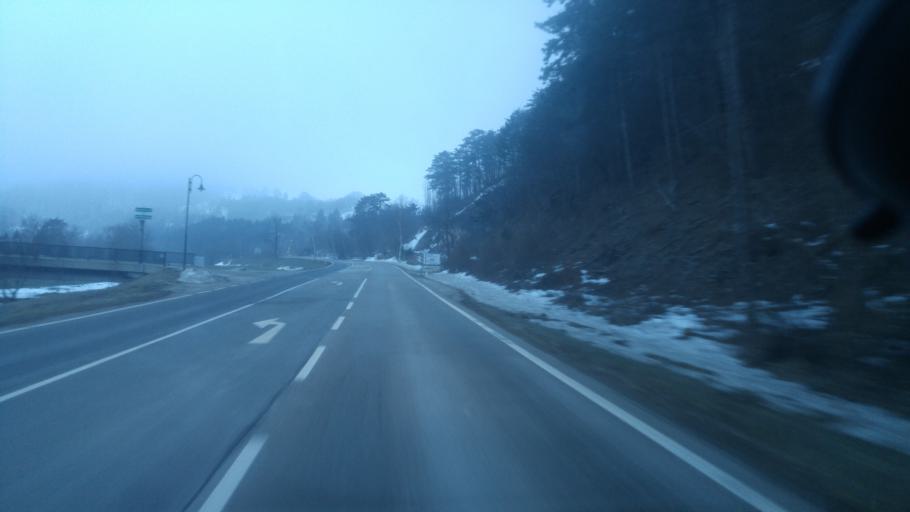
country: AT
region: Lower Austria
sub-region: Politischer Bezirk Baden
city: Altenmarkt an der Triesting
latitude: 48.0126
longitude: 16.0082
